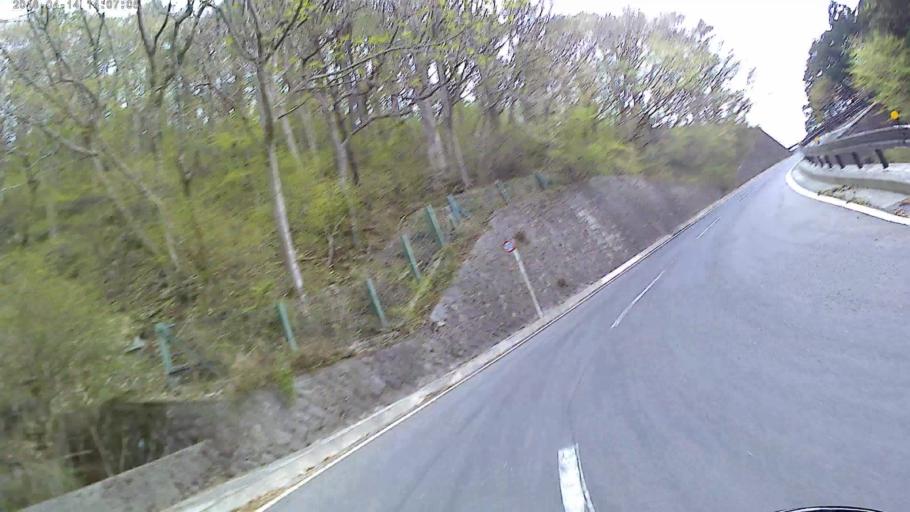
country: JP
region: Shizuoka
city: Gotemba
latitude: 35.3204
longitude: 139.0165
